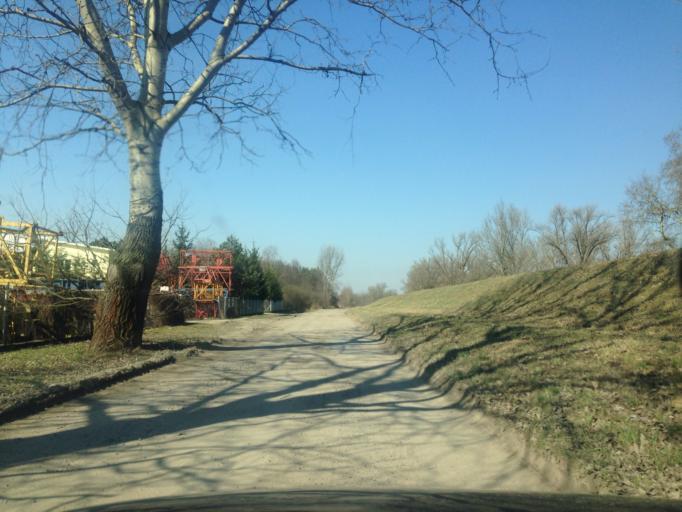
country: PL
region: Masovian Voivodeship
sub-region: Warszawa
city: Wawer
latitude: 52.1407
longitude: 21.1578
